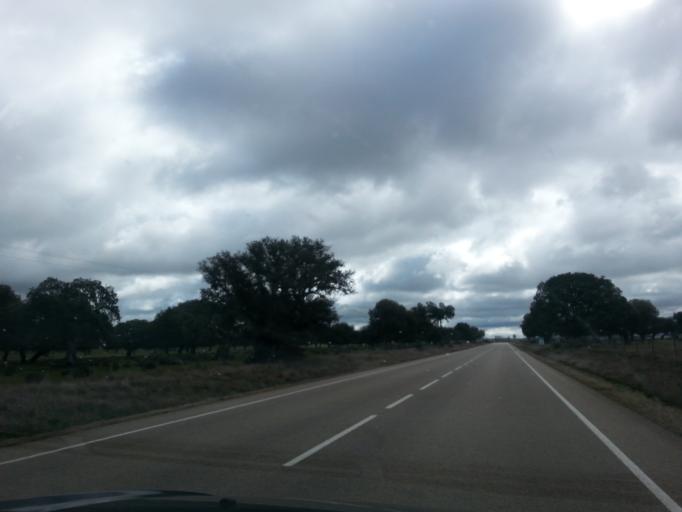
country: ES
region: Castille and Leon
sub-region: Provincia de Salamanca
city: Abusejo
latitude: 40.7256
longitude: -6.1558
